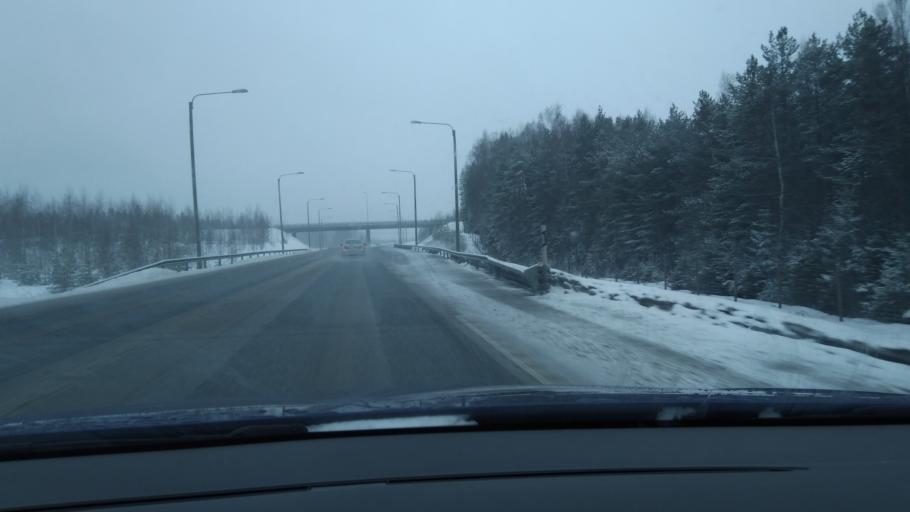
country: FI
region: Pirkanmaa
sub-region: Tampere
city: Kangasala
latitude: 61.5374
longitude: 23.9845
